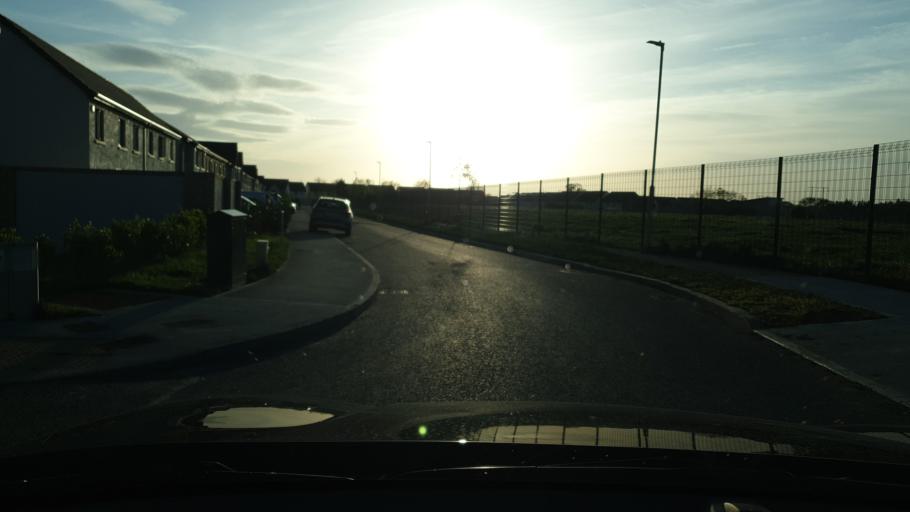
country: IE
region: Leinster
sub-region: Fingal County
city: Blanchardstown
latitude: 53.4224
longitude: -6.3713
